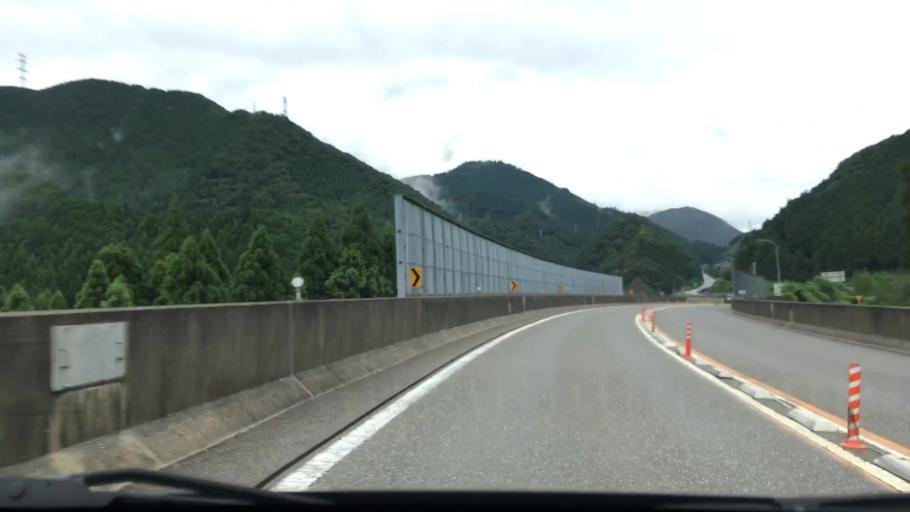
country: JP
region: Hyogo
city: Nishiwaki
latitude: 35.1932
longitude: 134.7908
